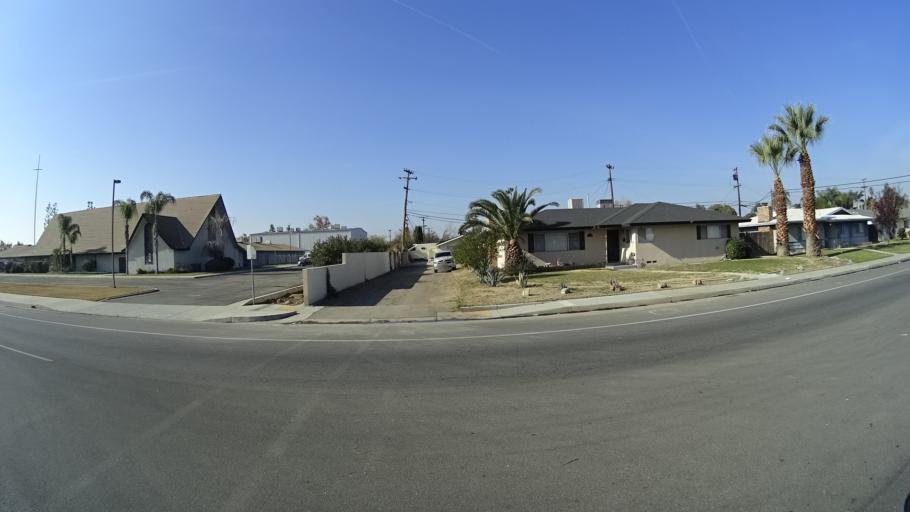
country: US
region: California
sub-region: Kern County
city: Bakersfield
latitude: 35.3304
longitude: -119.0300
